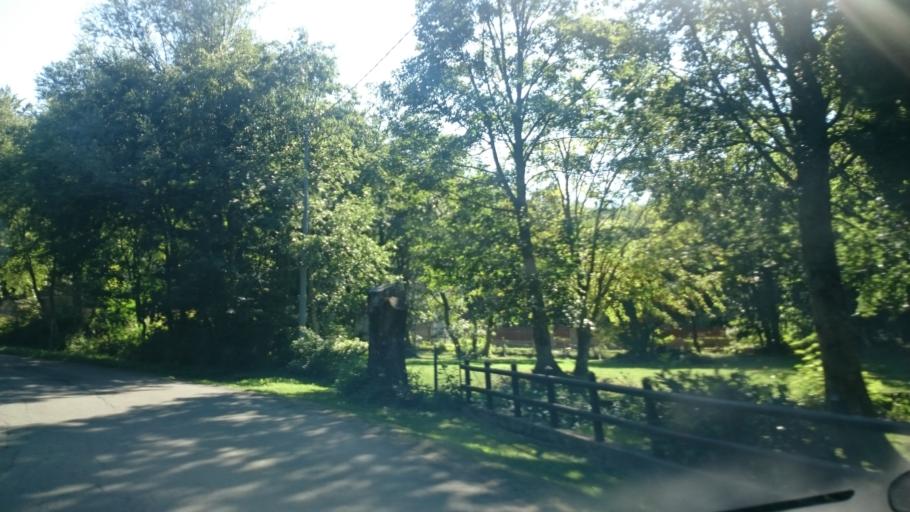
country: IT
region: Emilia-Romagna
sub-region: Provincia di Reggio Emilia
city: Villa Minozzo
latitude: 44.3040
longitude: 10.4274
